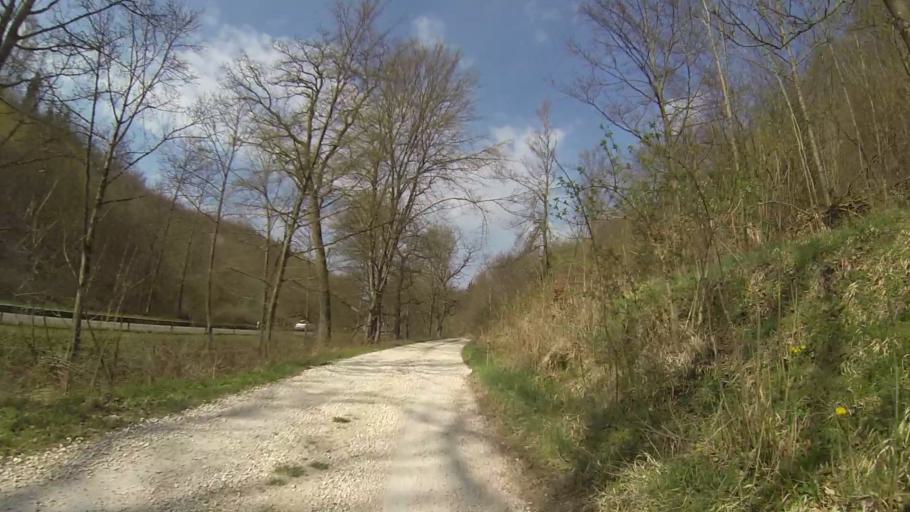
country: DE
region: Baden-Wuerttemberg
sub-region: Regierungsbezirk Stuttgart
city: Heidenheim an der Brenz
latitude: 48.6678
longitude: 10.1926
